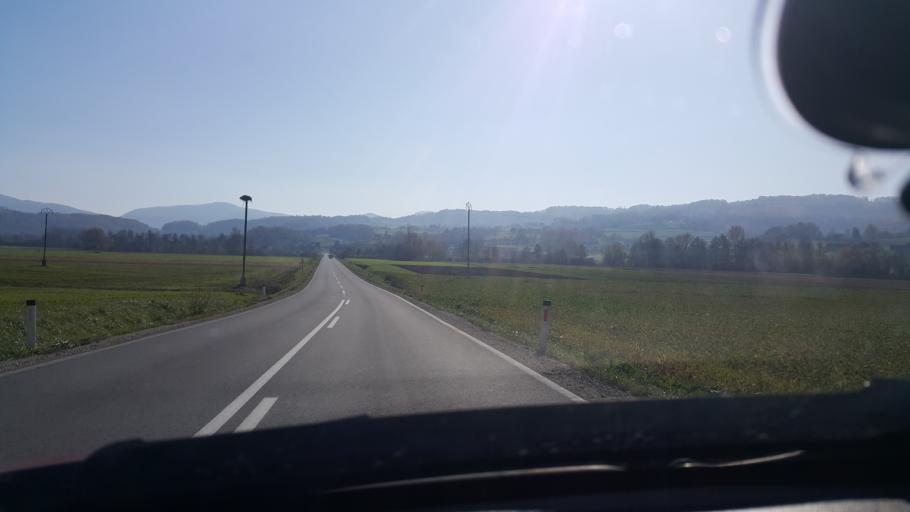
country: SI
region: Kozje
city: Kozje
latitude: 46.0989
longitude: 15.6119
